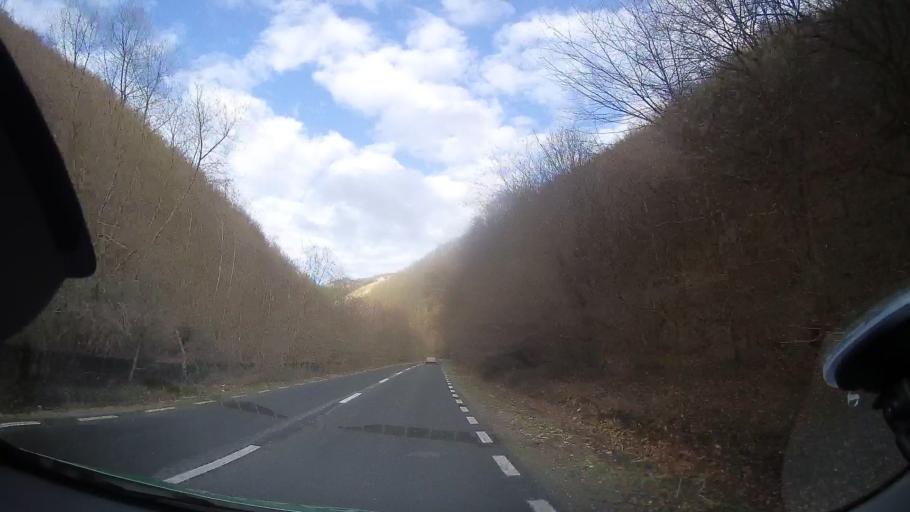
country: RO
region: Cluj
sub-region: Comuna Baisoara
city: Baisoara
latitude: 46.5888
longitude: 23.4418
